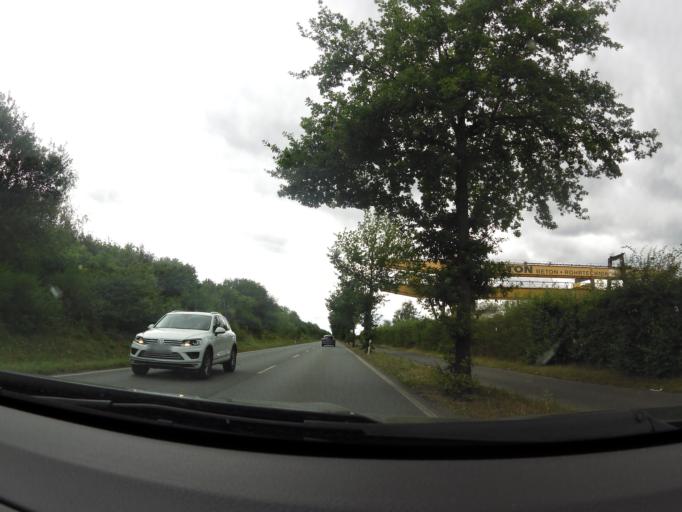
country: DE
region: North Rhine-Westphalia
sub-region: Regierungsbezirk Dusseldorf
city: Voerde
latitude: 51.6296
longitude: 6.7048
